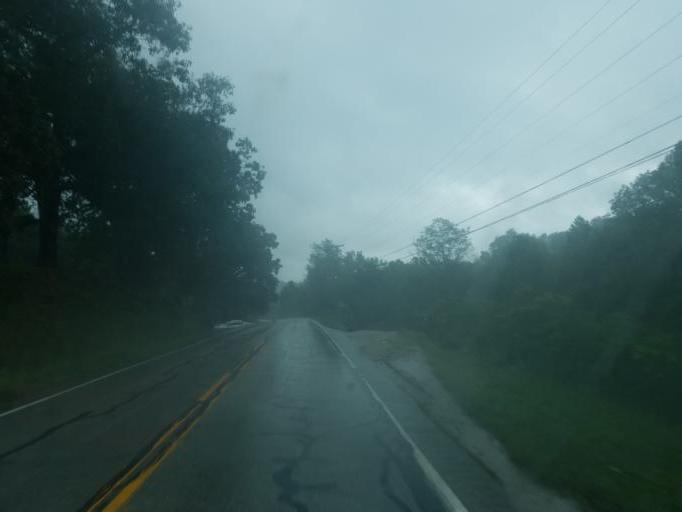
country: US
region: Kentucky
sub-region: Carter County
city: Olive Hill
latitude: 38.2931
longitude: -83.2861
